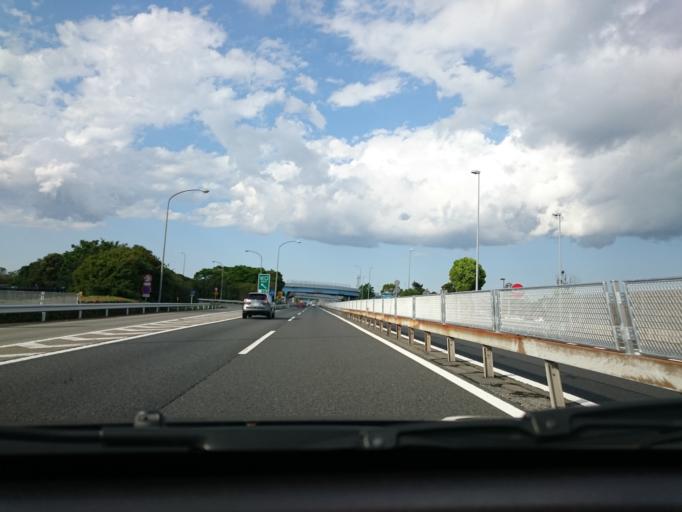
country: JP
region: Kanagawa
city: Isehara
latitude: 35.3623
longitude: 139.3054
